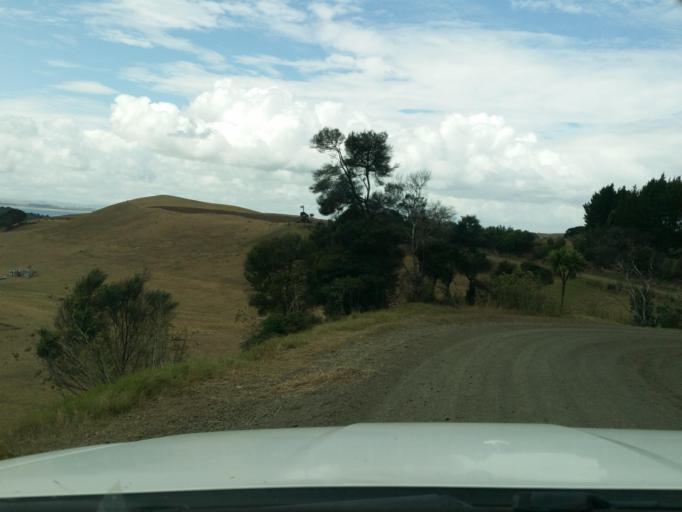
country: NZ
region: Auckland
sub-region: Auckland
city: Wellsford
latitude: -36.3337
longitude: 174.1552
